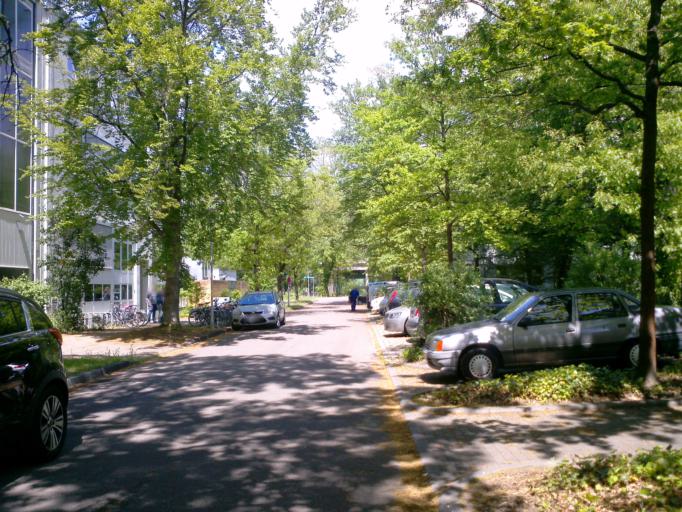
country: DE
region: Baden-Wuerttemberg
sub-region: Karlsruhe Region
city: Karlsruhe
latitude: 49.0145
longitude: 8.4155
